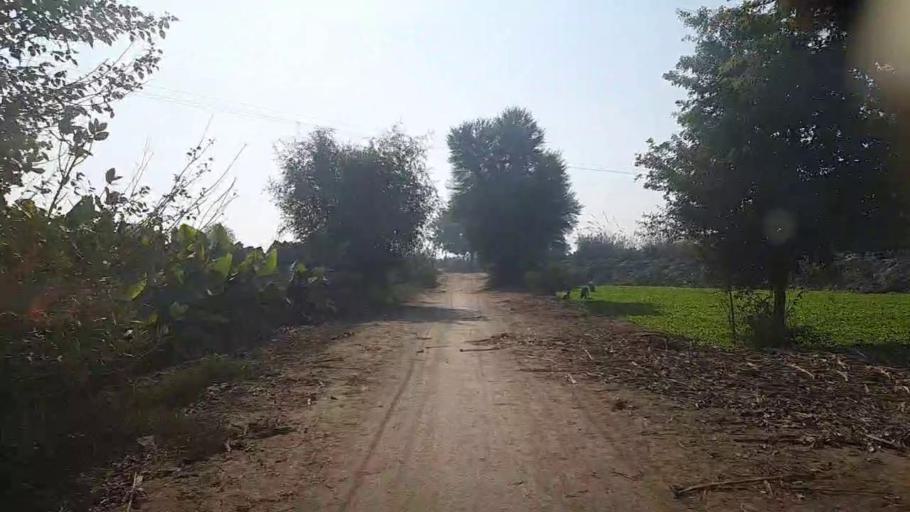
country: PK
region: Sindh
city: Kandiari
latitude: 27.0138
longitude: 68.5018
